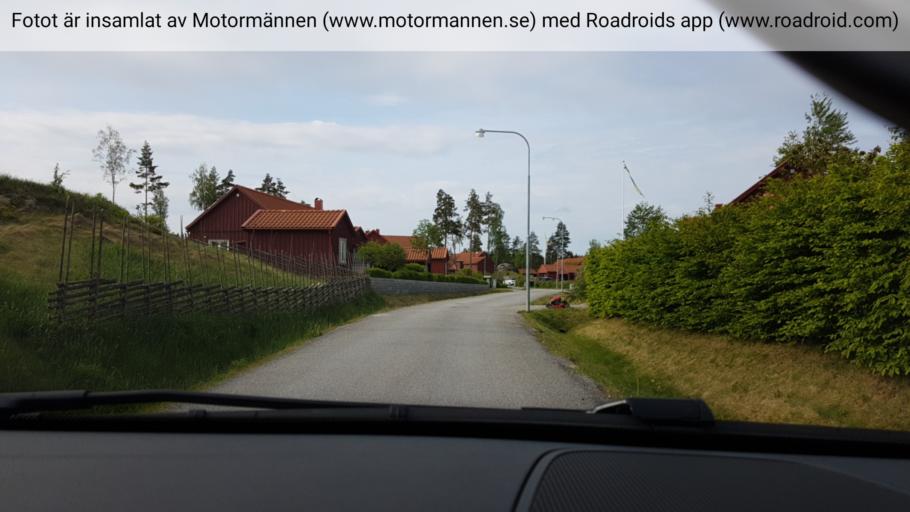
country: SE
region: Stockholm
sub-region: Nynashamns Kommun
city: Osmo
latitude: 59.0266
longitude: 17.9410
